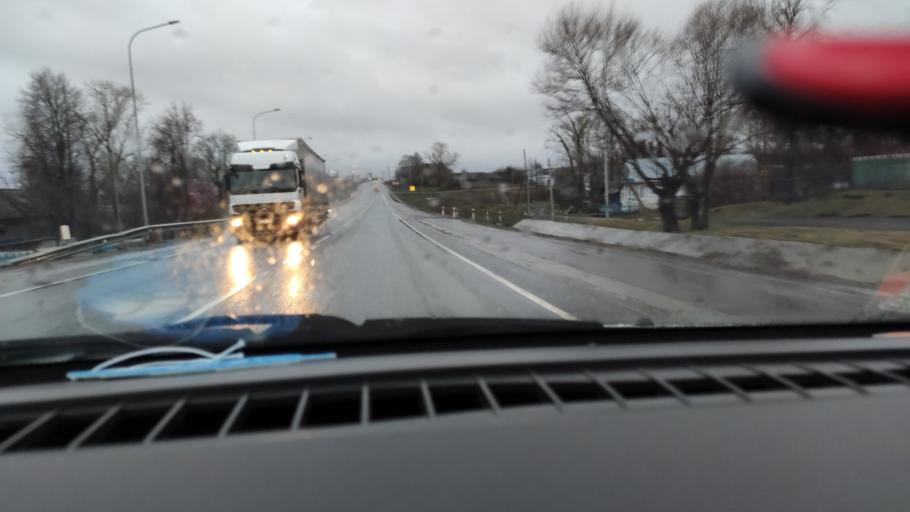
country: RU
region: Tatarstan
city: Mendeleyevsk
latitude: 56.0301
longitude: 52.3749
